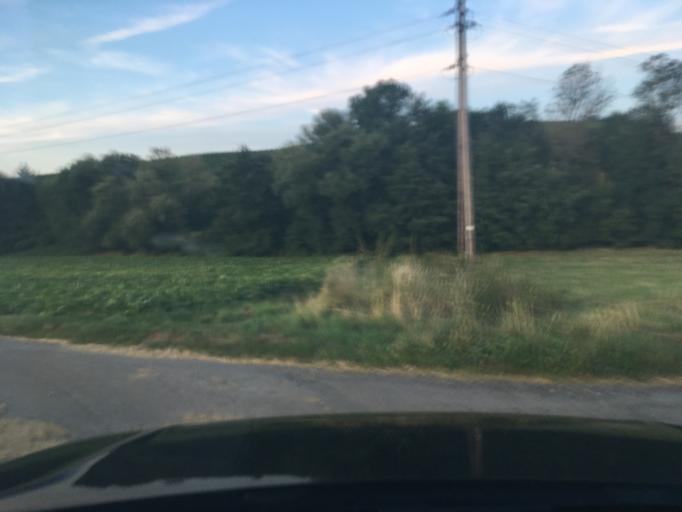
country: DE
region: Baden-Wuerttemberg
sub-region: Regierungsbezirk Stuttgart
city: Schwaigern
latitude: 49.1298
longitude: 9.0564
